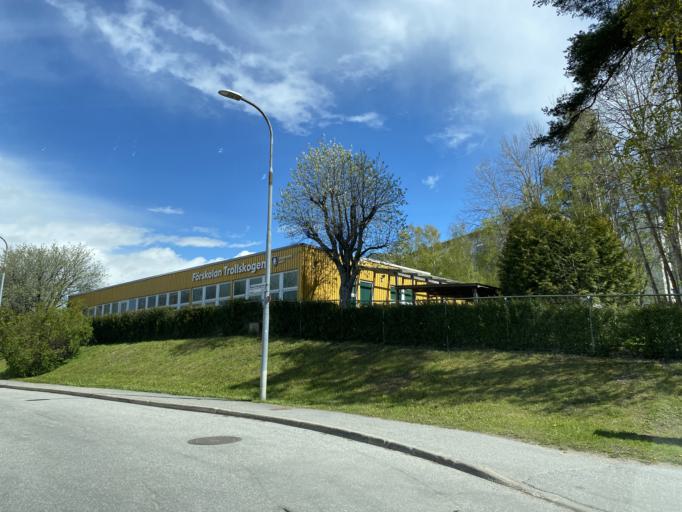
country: SE
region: Stockholm
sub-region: Stockholms Kommun
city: Kista
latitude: 59.4097
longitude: 17.9182
